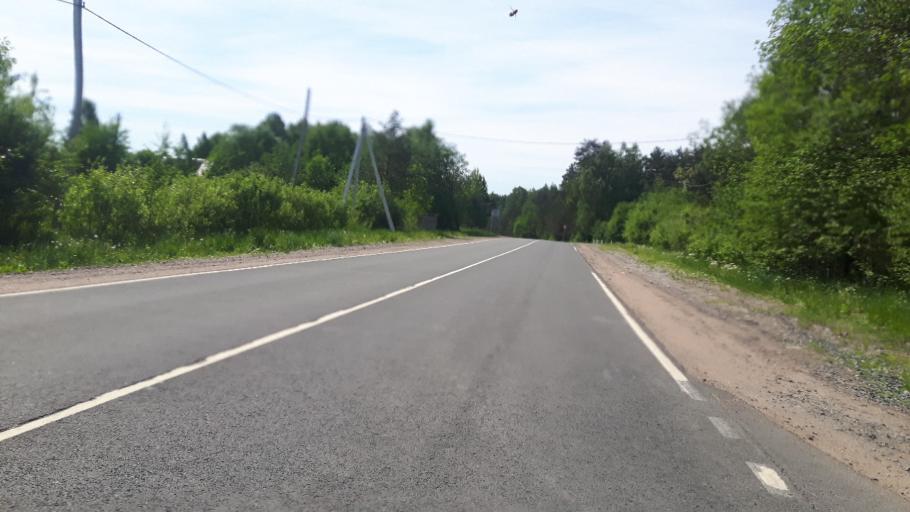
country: RU
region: Leningrad
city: Vistino
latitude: 59.6730
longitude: 28.4492
